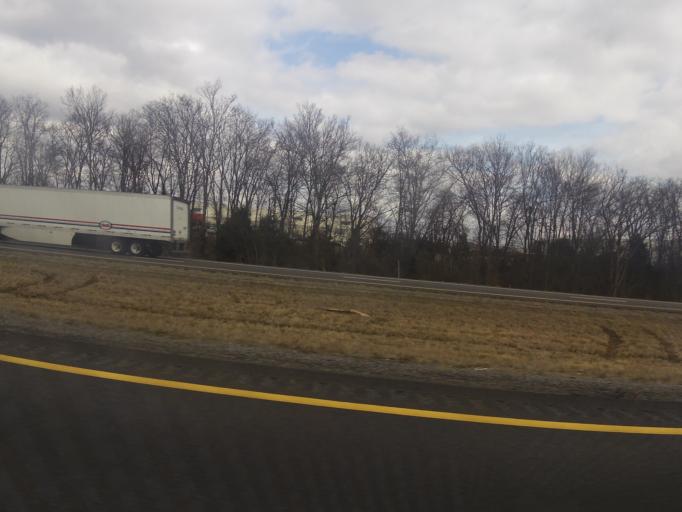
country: US
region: Tennessee
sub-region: Rutherford County
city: Murfreesboro
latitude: 35.7795
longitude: -86.3689
